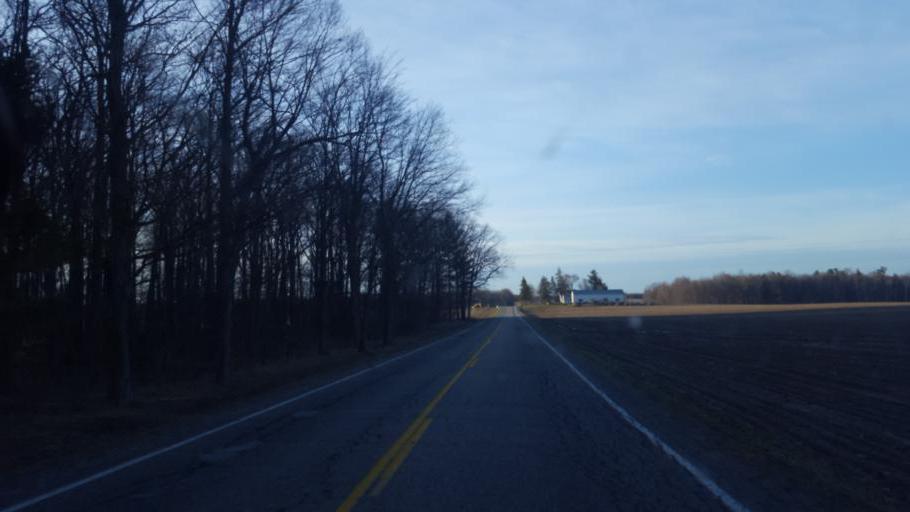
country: US
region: Michigan
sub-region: Montcalm County
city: Edmore
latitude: 43.4945
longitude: -85.0254
